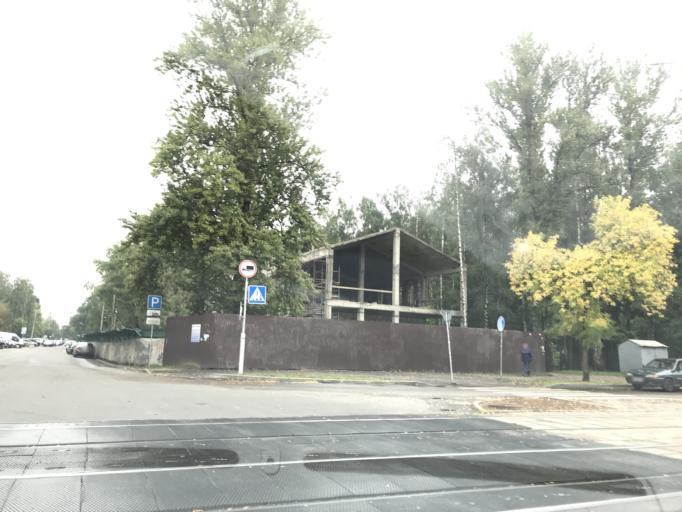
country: BY
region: Minsk
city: Minsk
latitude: 53.9469
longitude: 27.6135
